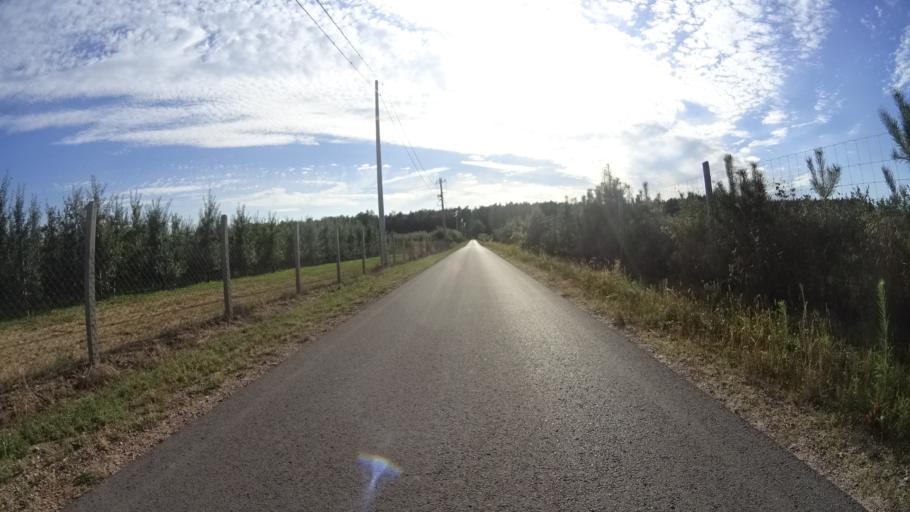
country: PL
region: Masovian Voivodeship
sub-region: Powiat bialobrzeski
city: Wysmierzyce
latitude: 51.6762
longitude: 20.8128
